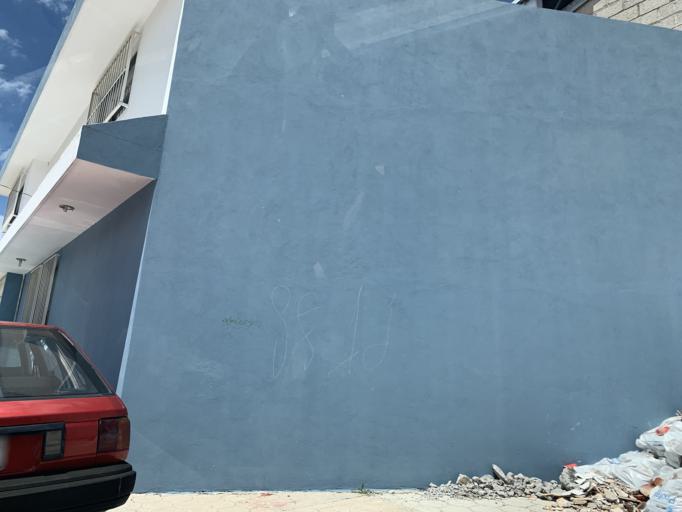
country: MX
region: Puebla
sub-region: Cuautlancingo
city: La Trinidad Chautenco
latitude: 19.0870
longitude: -98.2626
